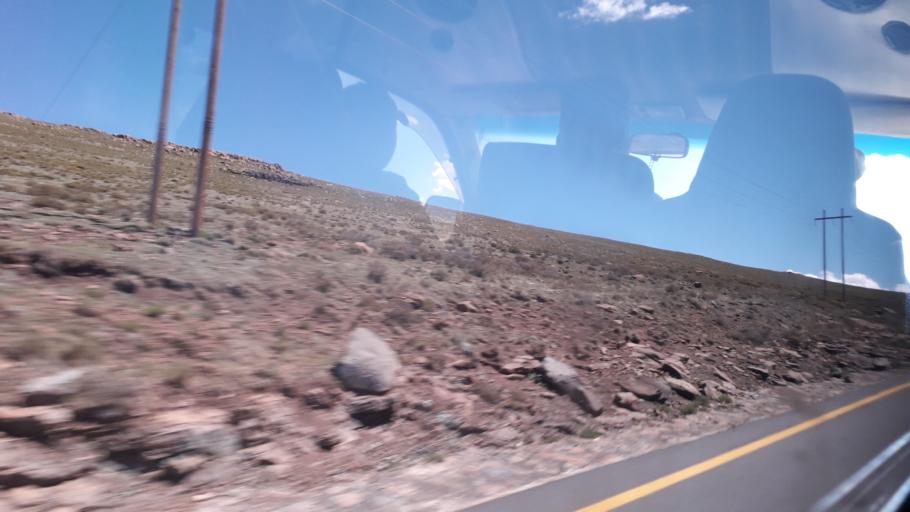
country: LS
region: Mokhotlong
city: Mokhotlong
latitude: -29.0524
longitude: 28.8517
